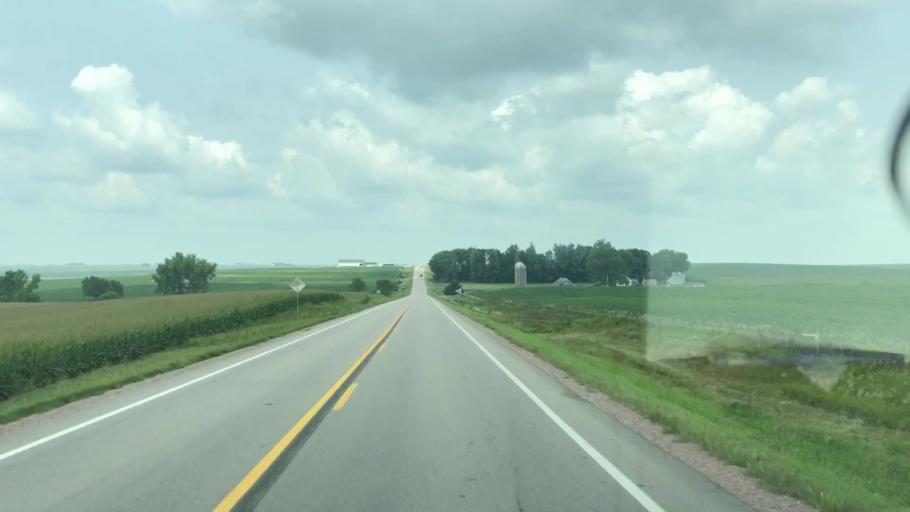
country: US
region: Iowa
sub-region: Plymouth County
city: Kingsley
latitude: 42.5944
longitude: -95.9573
